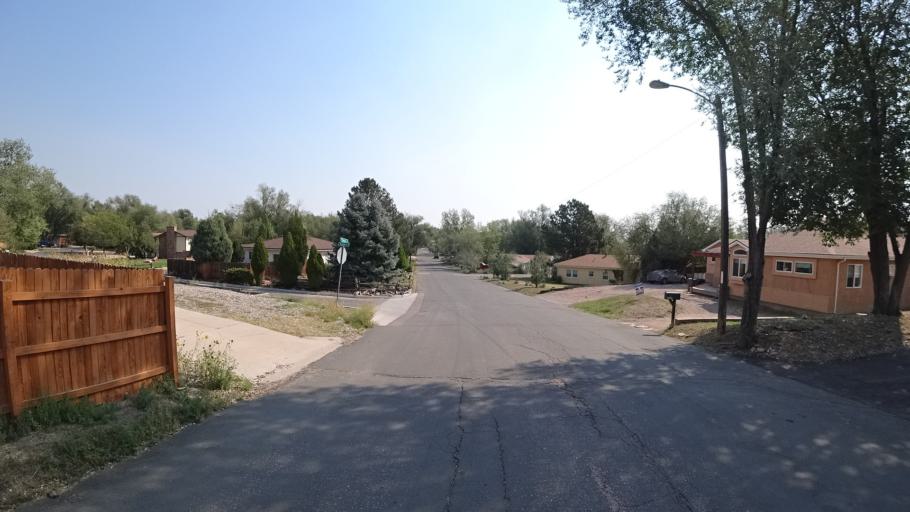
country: US
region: Colorado
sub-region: El Paso County
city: Colorado Springs
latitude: 38.8107
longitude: -104.8396
